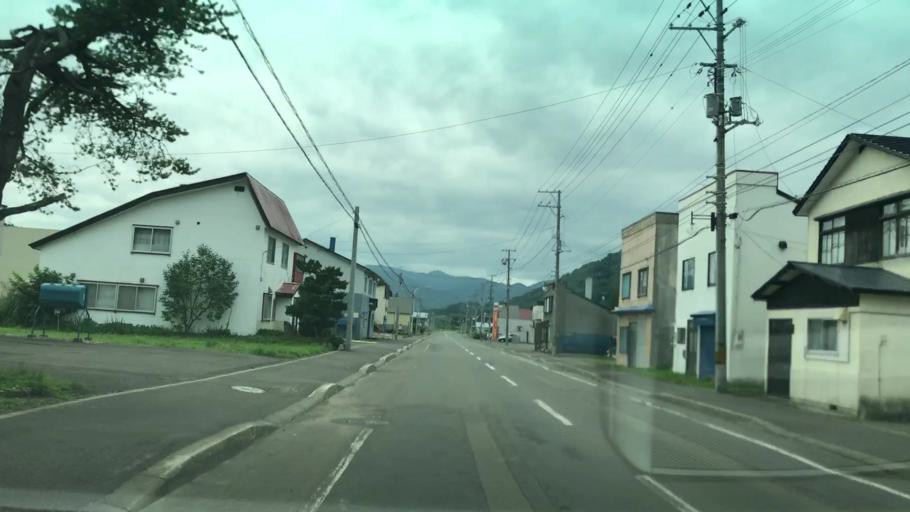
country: JP
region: Hokkaido
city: Yoichi
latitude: 43.0837
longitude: 140.8160
